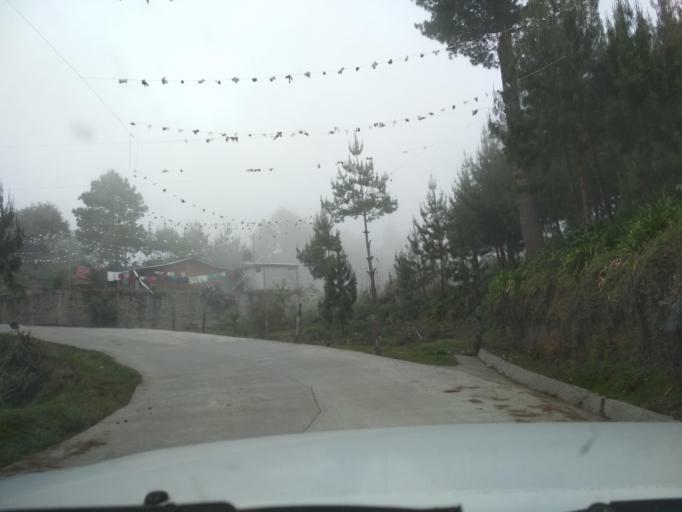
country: MX
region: Veracruz
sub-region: La Perla
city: Chilapa
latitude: 18.9827
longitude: -97.1964
